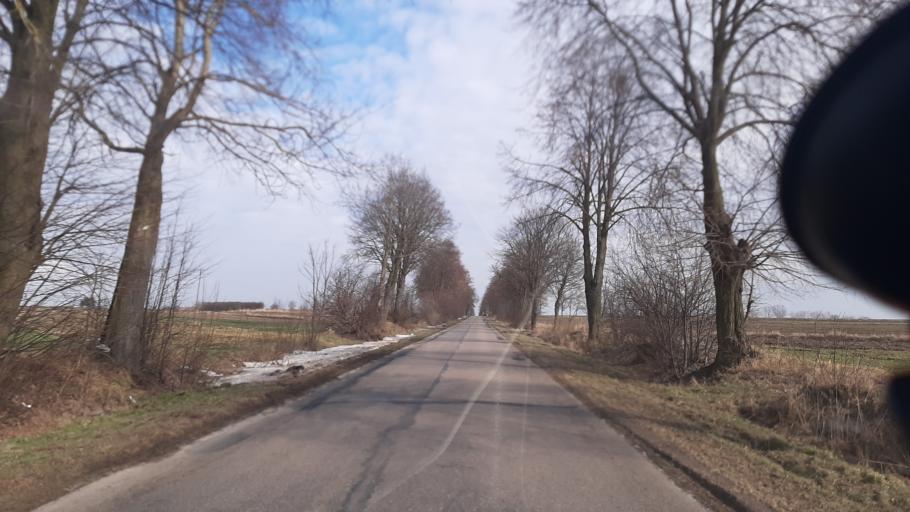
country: PL
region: Lublin Voivodeship
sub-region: Powiat lubartowski
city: Wola Sernicka
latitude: 51.4558
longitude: 22.6848
